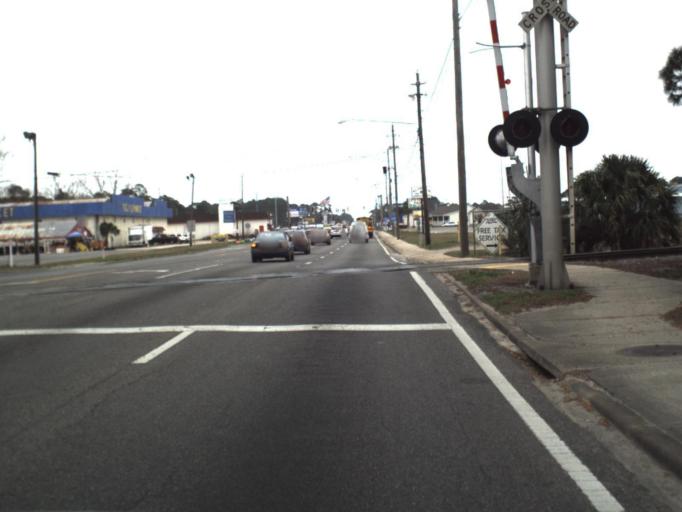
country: US
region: Florida
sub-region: Bay County
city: Cedar Grove
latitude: 30.1749
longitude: -85.6360
